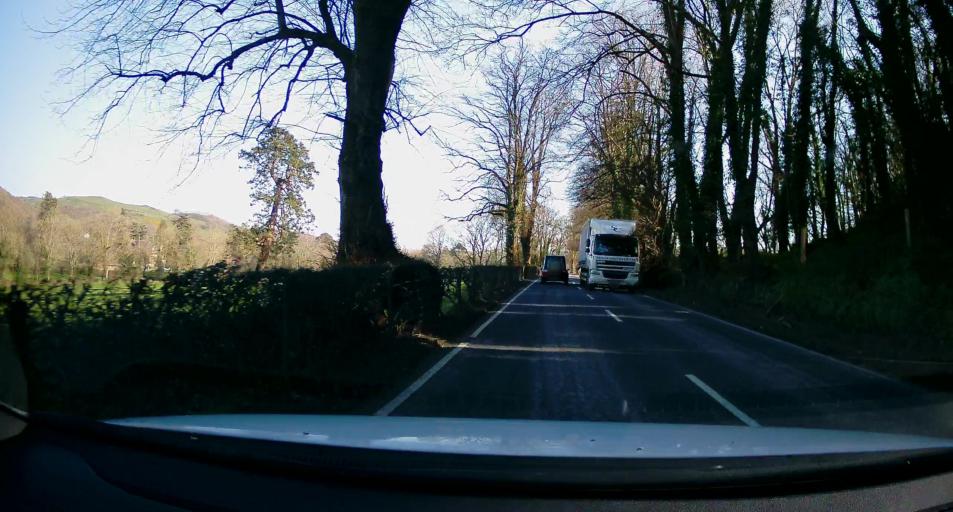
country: GB
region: Wales
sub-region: County of Ceredigion
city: Penparcau
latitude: 52.3649
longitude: -4.0616
